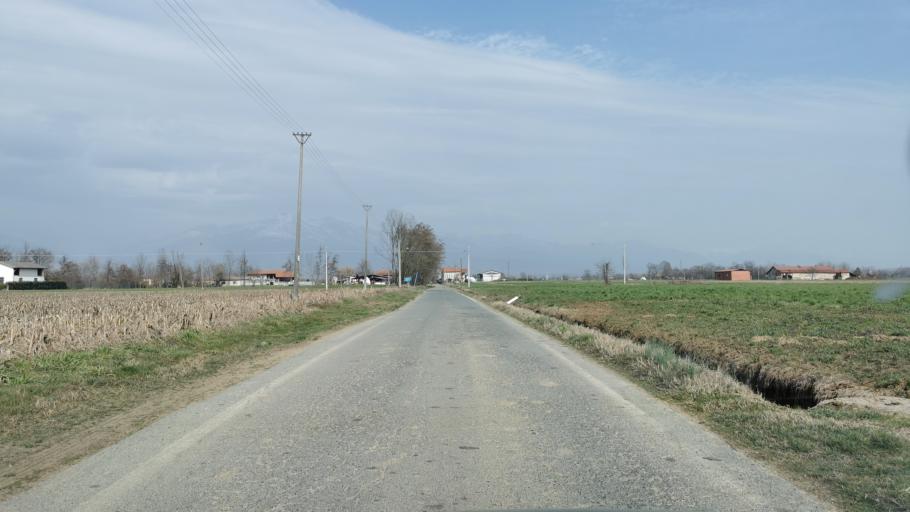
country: IT
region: Piedmont
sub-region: Provincia di Torino
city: Front
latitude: 45.2930
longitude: 7.6881
